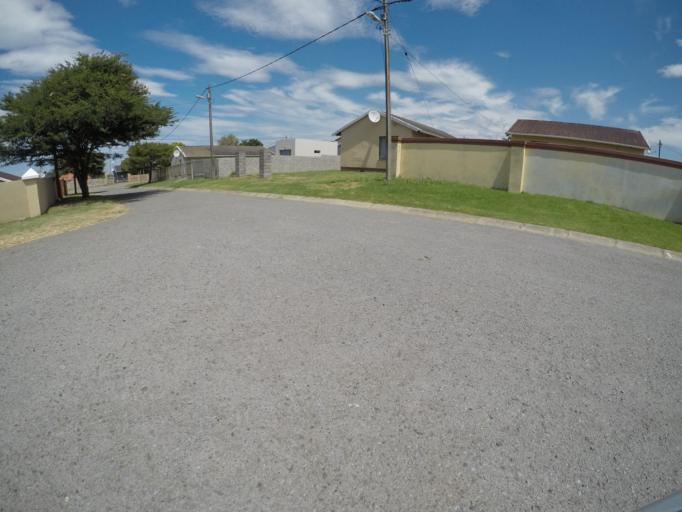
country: ZA
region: Eastern Cape
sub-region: Buffalo City Metropolitan Municipality
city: East London
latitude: -33.0435
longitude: 27.8686
